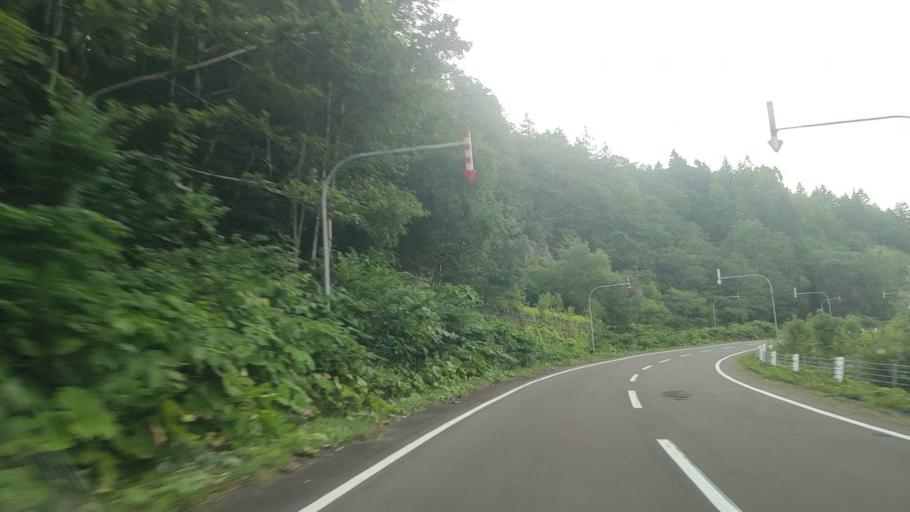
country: JP
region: Hokkaido
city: Bibai
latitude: 43.1301
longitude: 142.0953
